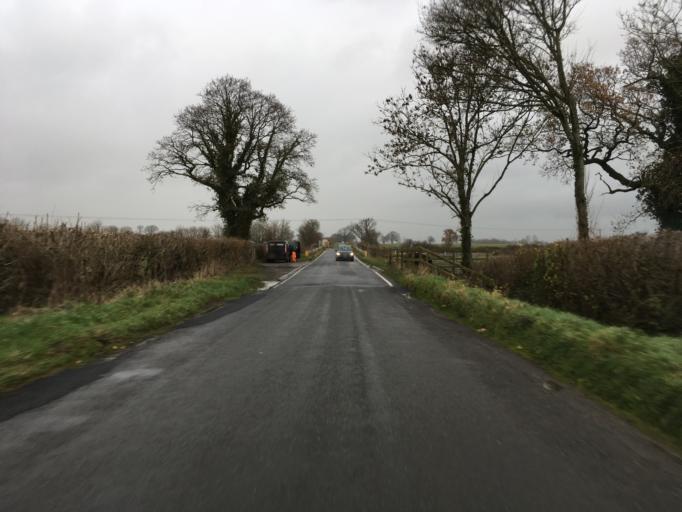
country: GB
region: England
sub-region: Wiltshire
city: Norton
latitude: 51.5436
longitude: -2.2009
